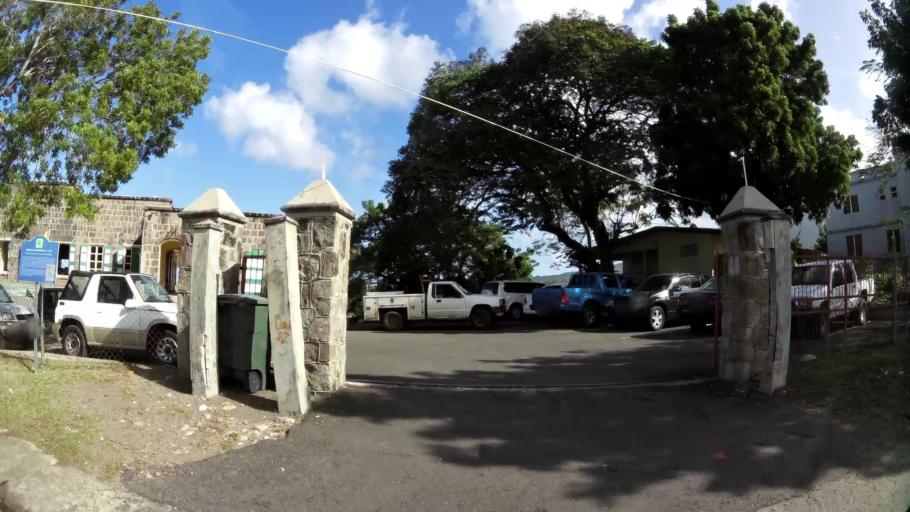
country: KN
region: Saint Paul Charlestown
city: Charlestown
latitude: 17.1321
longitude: -62.6256
